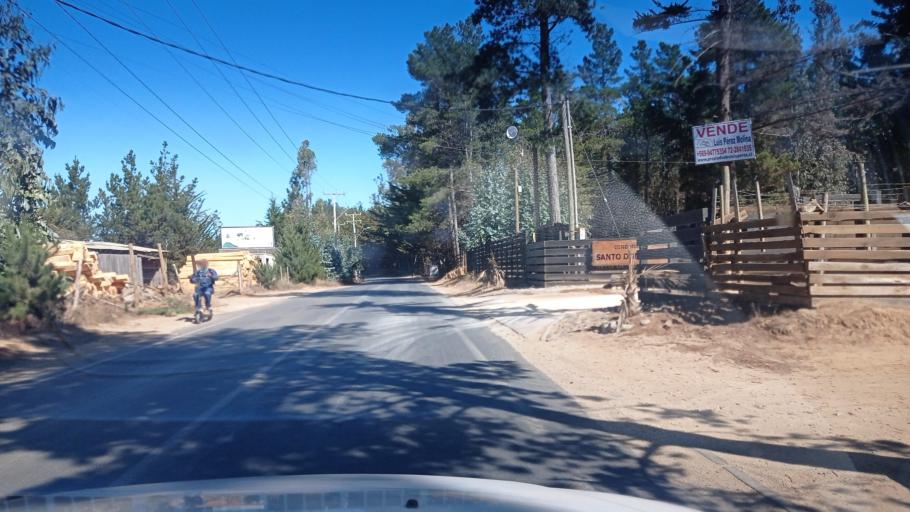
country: CL
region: O'Higgins
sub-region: Provincia de Colchagua
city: Santa Cruz
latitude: -34.4158
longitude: -71.9994
